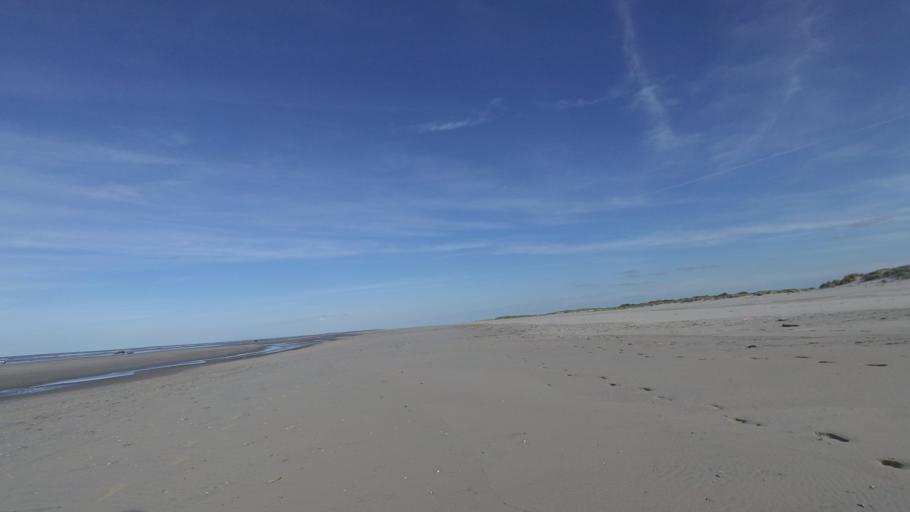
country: NL
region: Friesland
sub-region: Gemeente Dongeradeel
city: Ternaard
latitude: 53.4680
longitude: 5.9246
